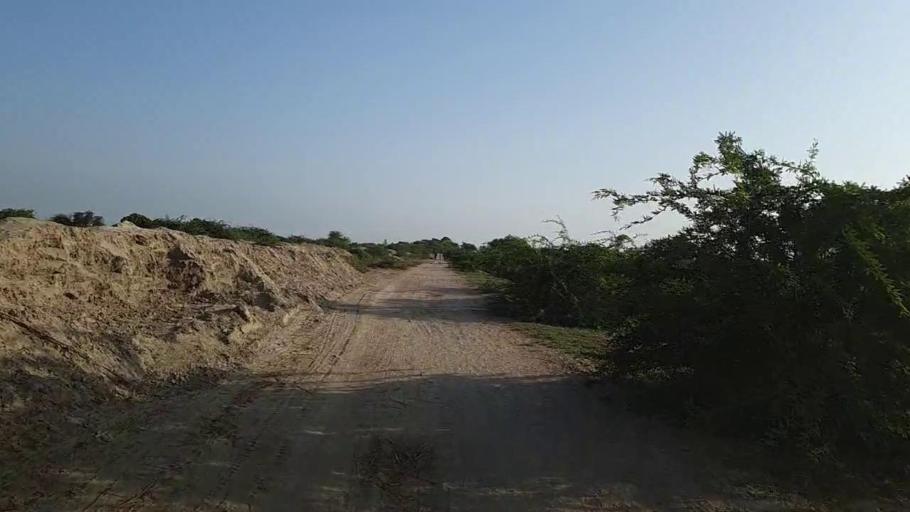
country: PK
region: Sindh
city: Kario
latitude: 24.7359
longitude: 68.6694
